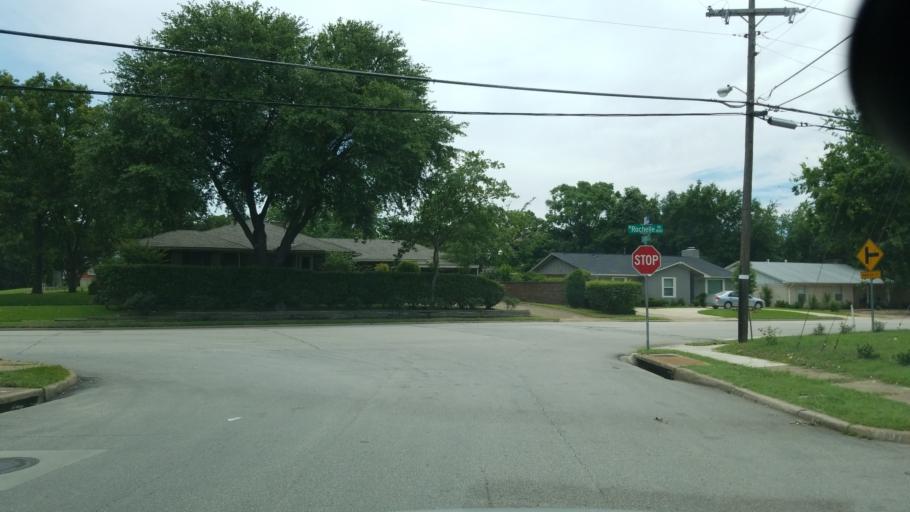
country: US
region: Texas
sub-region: Dallas County
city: Irving
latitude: 32.8438
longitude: -96.9682
